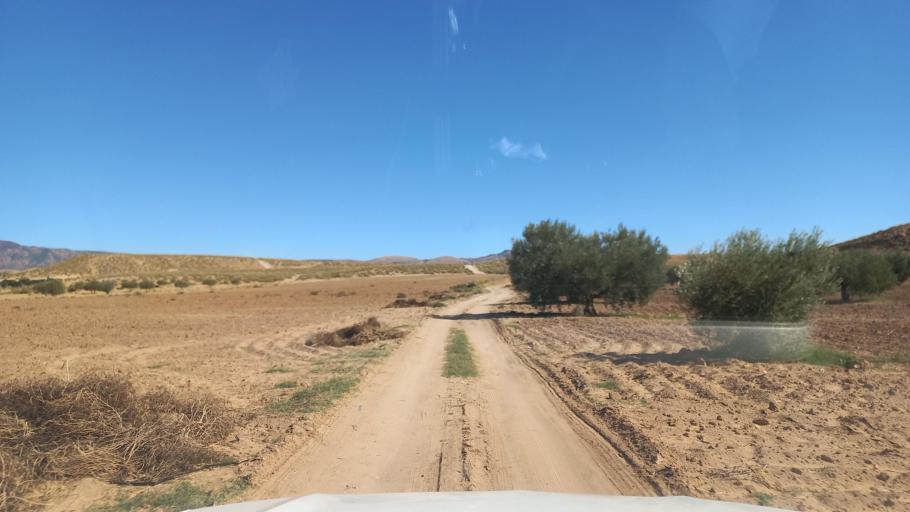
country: TN
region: Al Qasrayn
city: Sbiba
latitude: 35.4056
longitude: 9.0902
